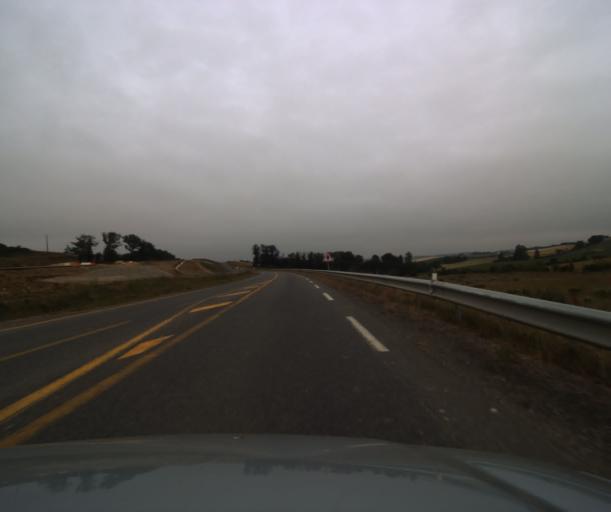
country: FR
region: Midi-Pyrenees
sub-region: Departement du Gers
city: Aubiet
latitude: 43.6482
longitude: 0.7050
